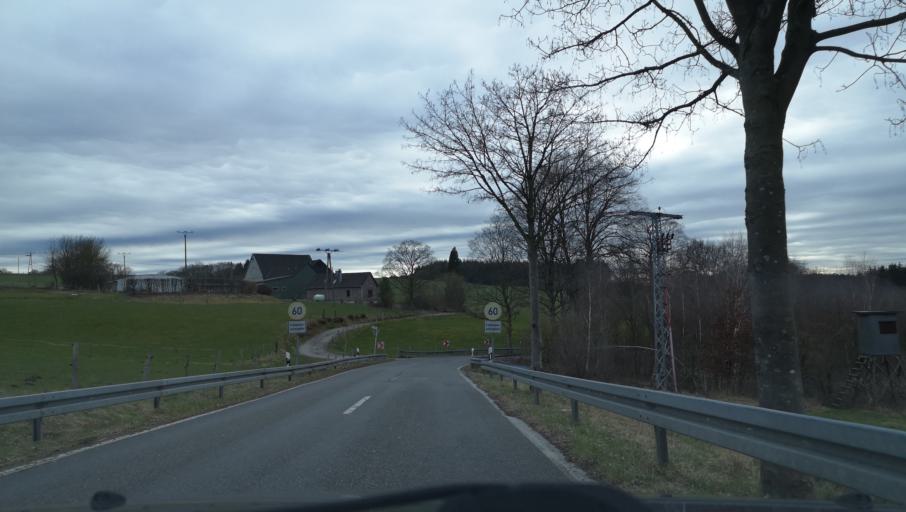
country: DE
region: North Rhine-Westphalia
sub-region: Regierungsbezirk Arnsberg
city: Schwelm
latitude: 51.2210
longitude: 7.2790
